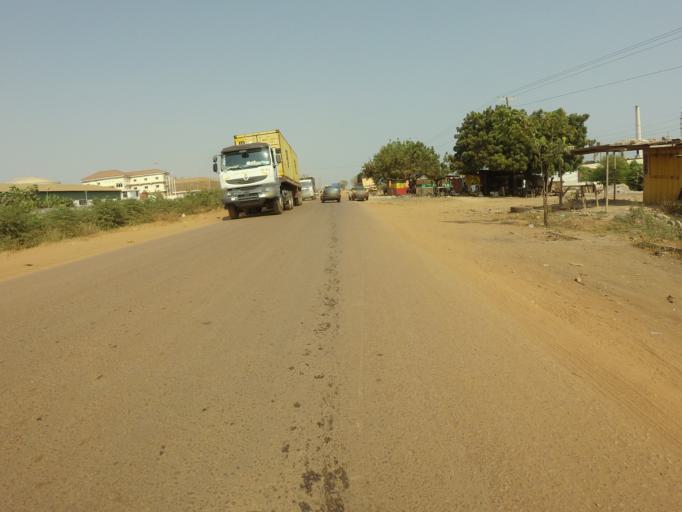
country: GH
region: Greater Accra
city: Tema
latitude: 5.6690
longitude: 0.0150
